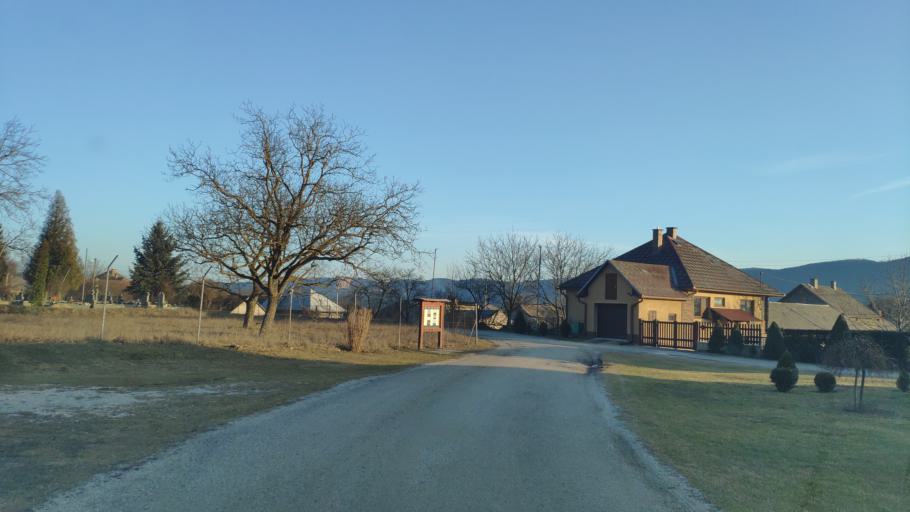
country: SK
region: Kosicky
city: Medzev
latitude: 48.6084
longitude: 20.7497
